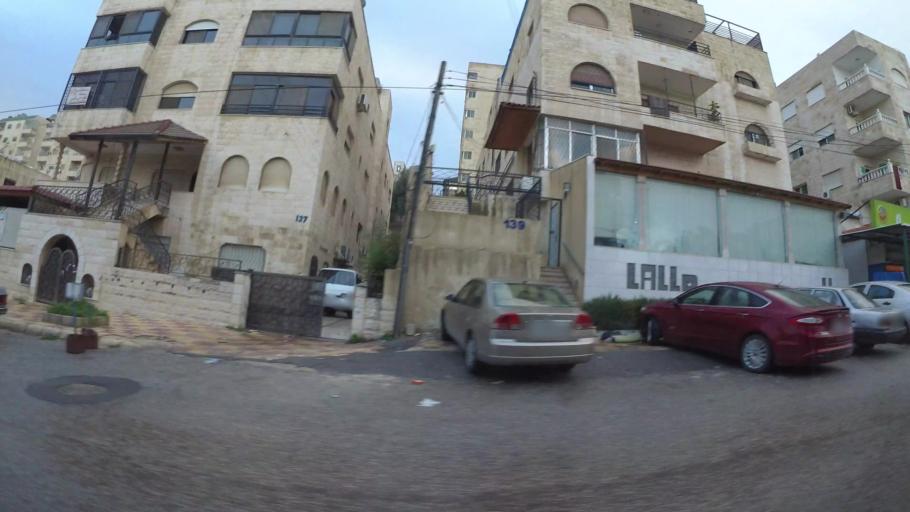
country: JO
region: Amman
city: Amman
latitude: 31.9867
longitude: 35.9158
